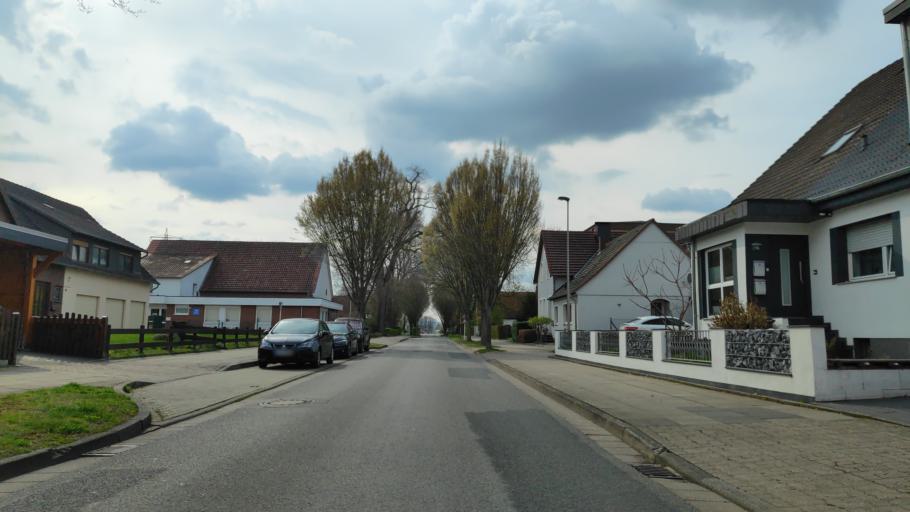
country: DE
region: North Rhine-Westphalia
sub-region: Regierungsbezirk Detmold
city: Minden
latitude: 52.2864
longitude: 8.8818
